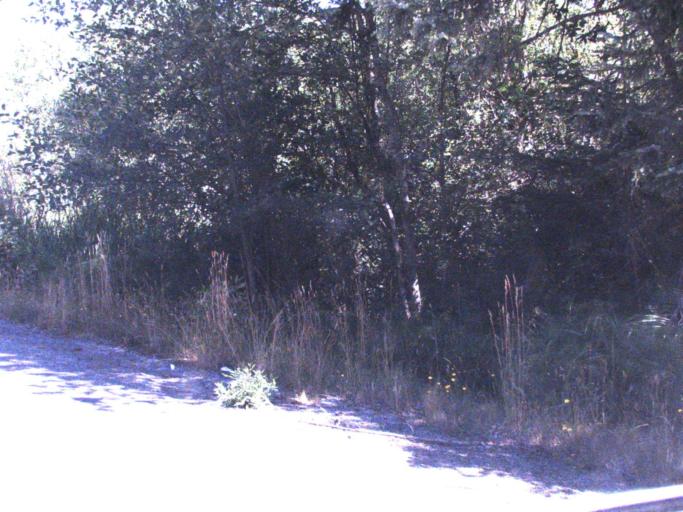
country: US
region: Washington
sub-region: King County
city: Enumclaw
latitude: 47.1818
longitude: -121.9228
